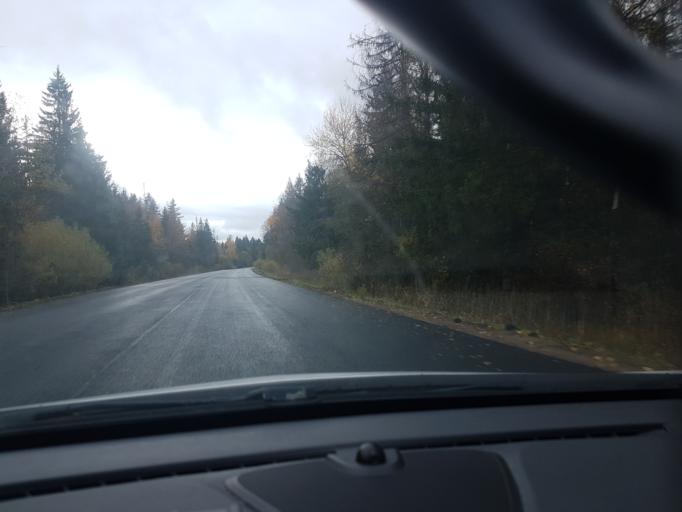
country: RU
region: Moskovskaya
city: Sychevo
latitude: 56.0040
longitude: 36.3160
